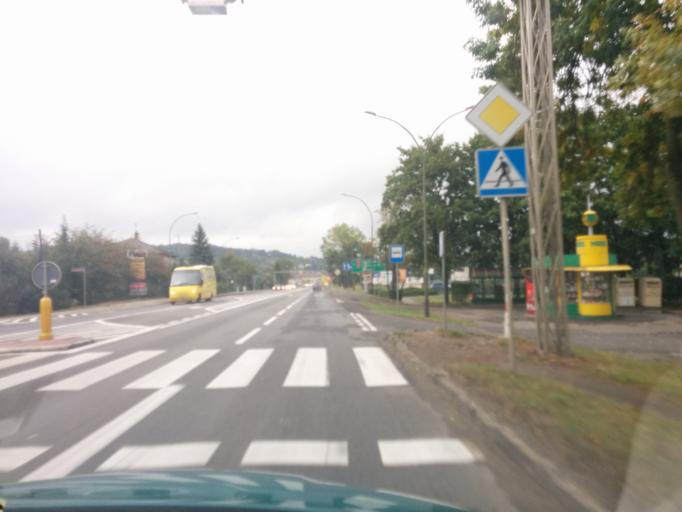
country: PL
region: Subcarpathian Voivodeship
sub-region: Powiat sanocki
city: Sanok
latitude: 49.5694
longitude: 22.1571
